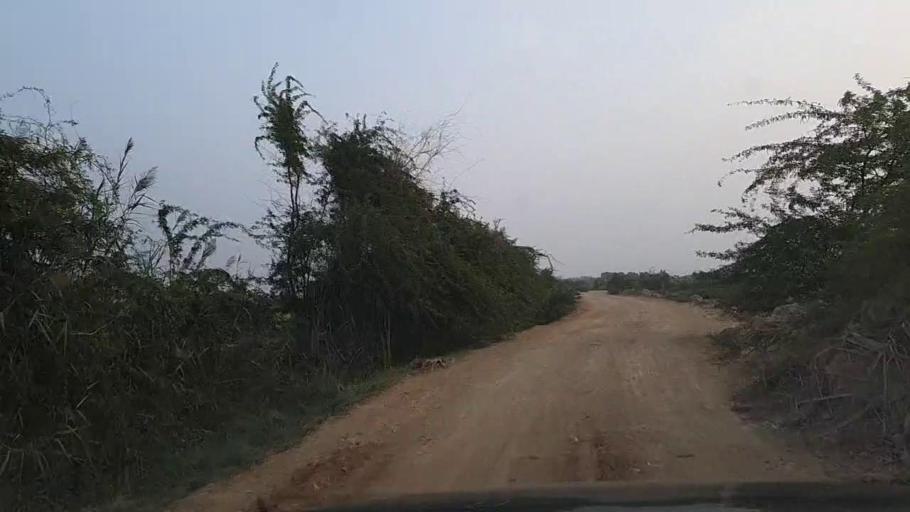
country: PK
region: Sindh
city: Gharo
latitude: 24.7386
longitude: 67.6942
